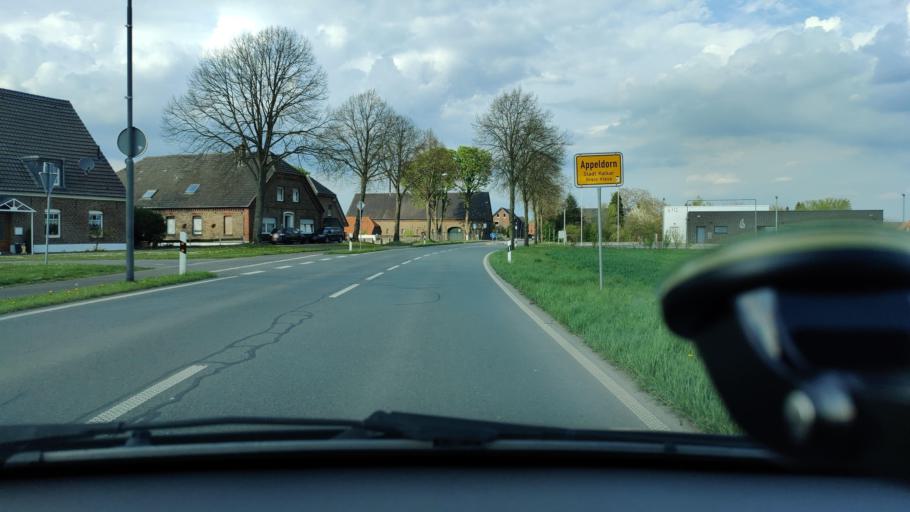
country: DE
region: North Rhine-Westphalia
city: Kalkar
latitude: 51.7170
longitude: 6.3419
